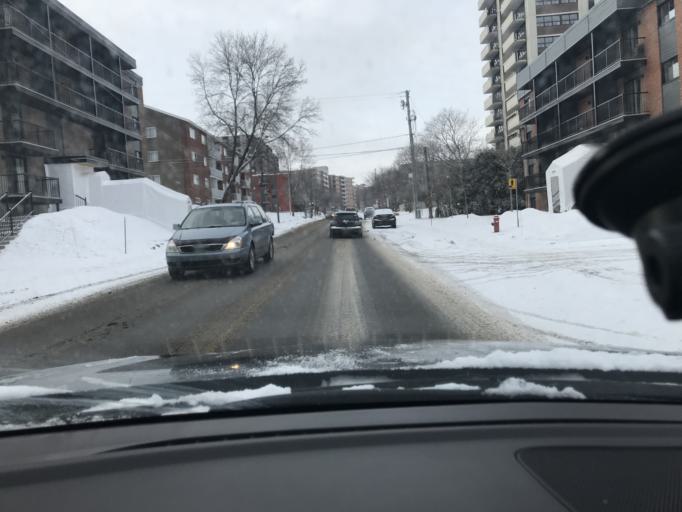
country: CA
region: Quebec
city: Quebec
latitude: 46.7899
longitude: -71.2757
